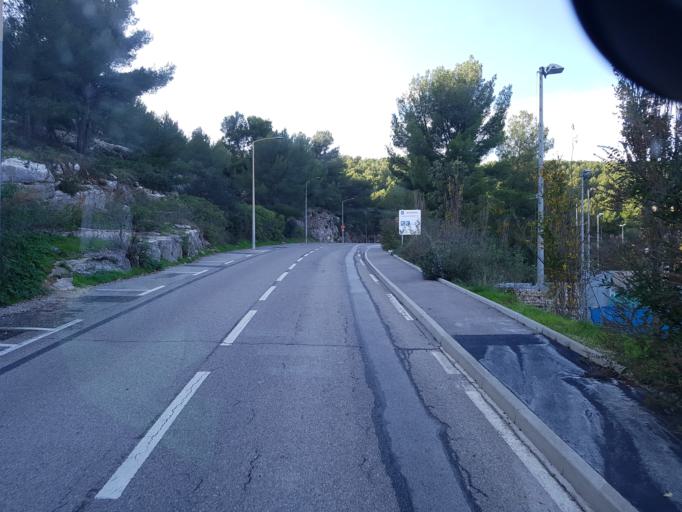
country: FR
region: Provence-Alpes-Cote d'Azur
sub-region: Departement des Bouches-du-Rhone
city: Cassis
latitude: 43.2293
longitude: 5.5343
